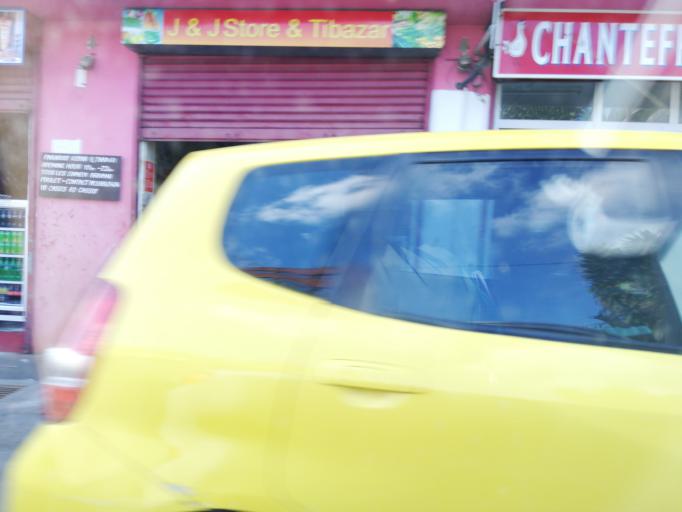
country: MU
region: Port Louis
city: Port Louis
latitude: -20.1639
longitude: 57.4824
